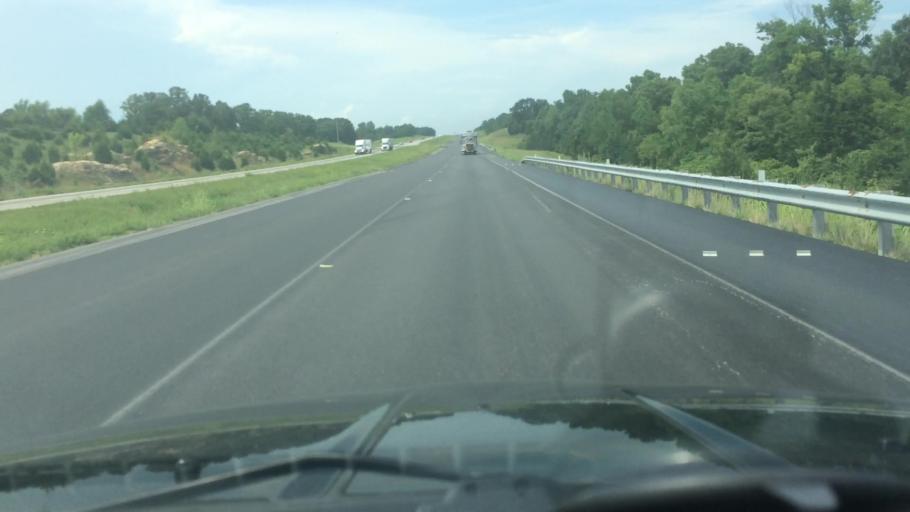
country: US
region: Missouri
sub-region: Saint Clair County
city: Osceola
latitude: 37.9574
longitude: -93.6424
